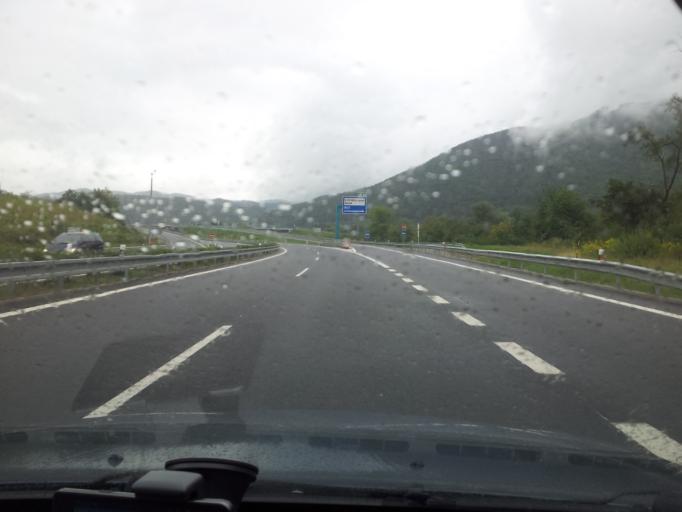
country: SK
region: Banskobystricky
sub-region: Okres Banska Bystrica
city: Banska Bystrica
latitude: 48.7413
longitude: 19.1820
